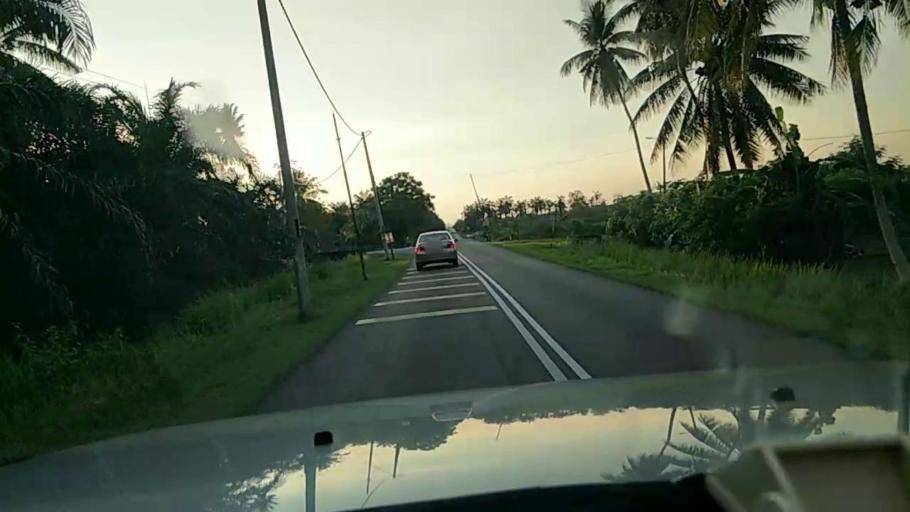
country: MY
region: Selangor
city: Kuala Selangor
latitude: 3.3155
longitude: 101.2823
